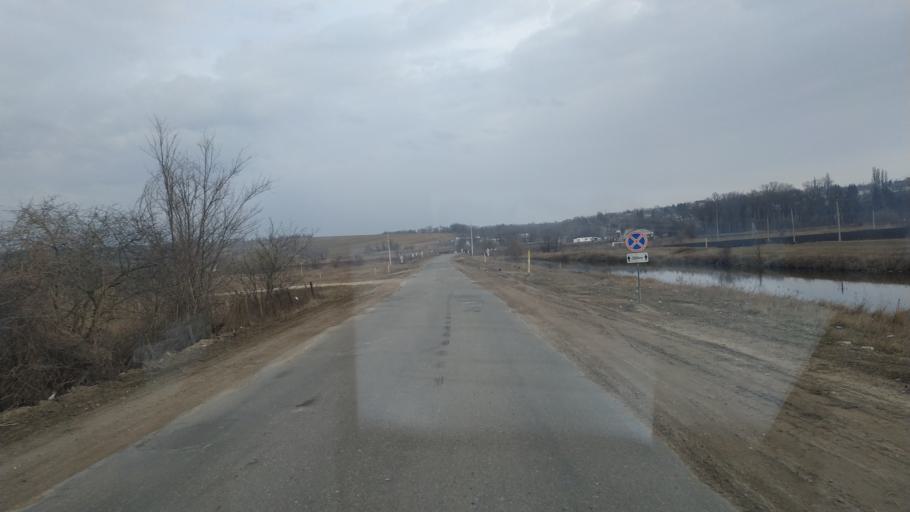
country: MD
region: Chisinau
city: Singera
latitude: 46.9207
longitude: 29.0464
